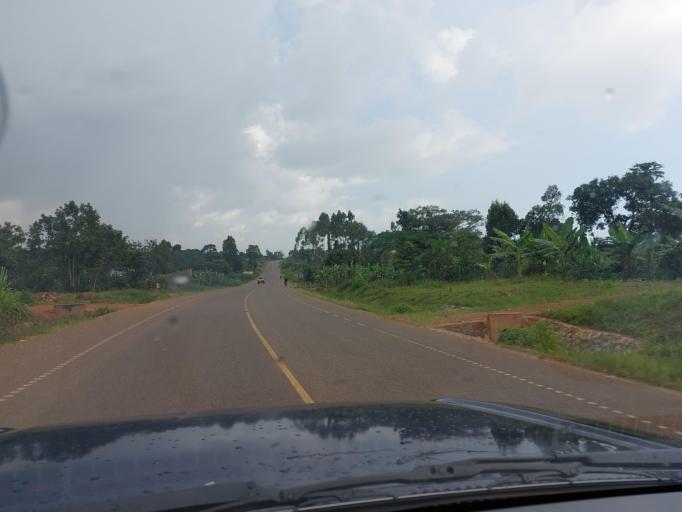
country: UG
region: Central Region
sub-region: Buikwe District
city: Buikwe
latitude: 0.2414
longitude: 32.9314
